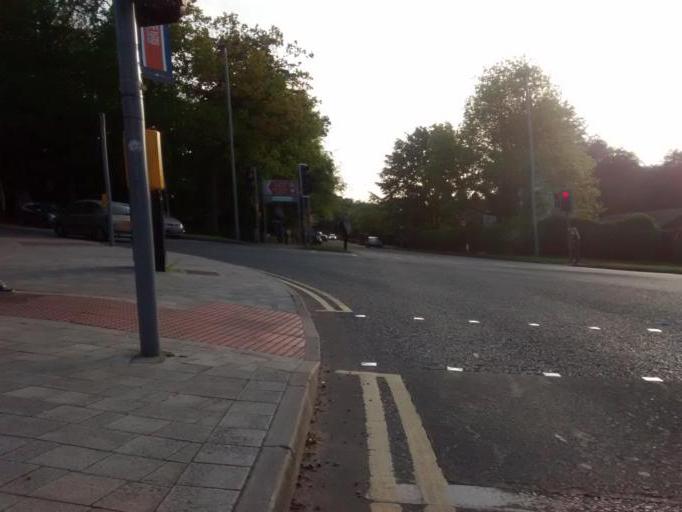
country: GB
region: England
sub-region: County Durham
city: Durham
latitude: 54.7687
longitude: -1.5739
